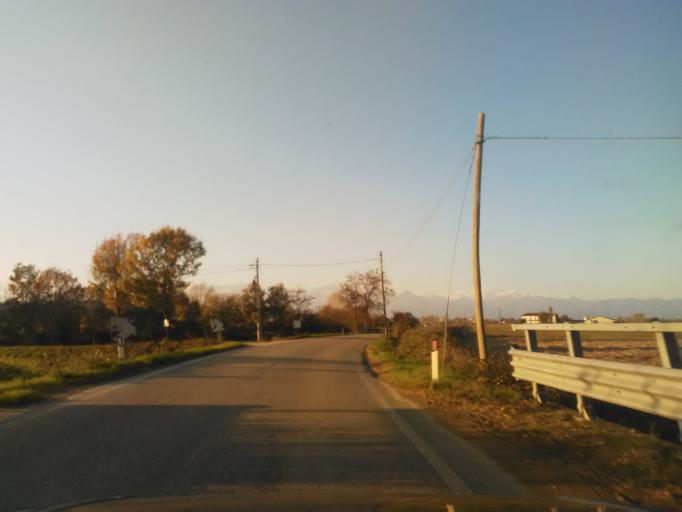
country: IT
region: Piedmont
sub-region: Provincia di Vercelli
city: Santhia
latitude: 45.4113
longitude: 8.1471
